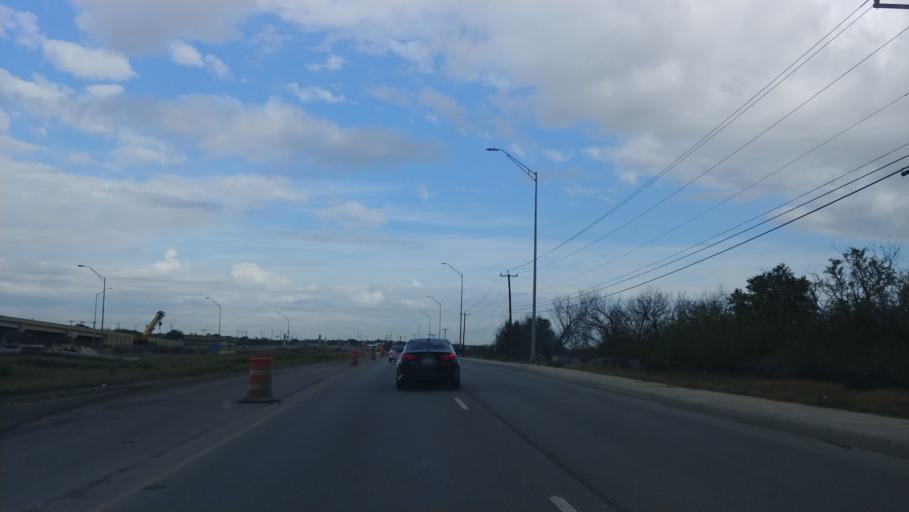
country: US
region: Texas
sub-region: Bexar County
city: Lackland Air Force Base
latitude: 29.3869
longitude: -98.7010
